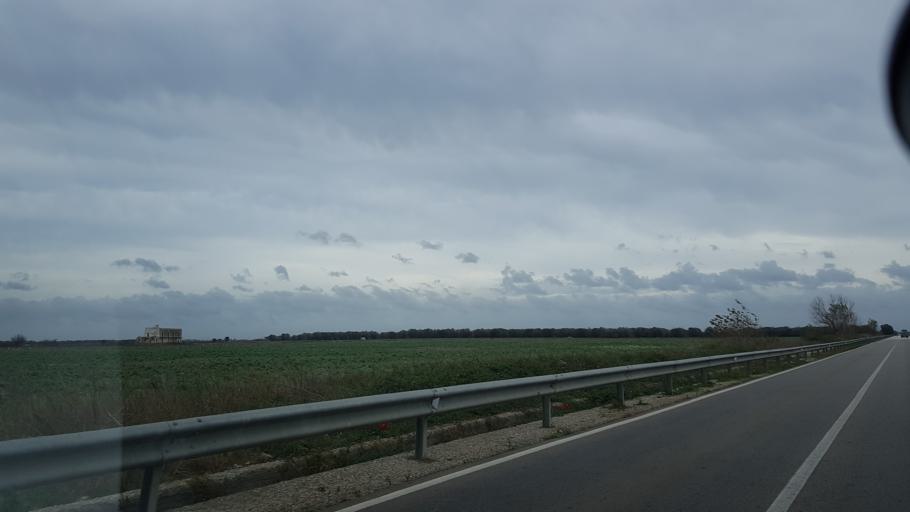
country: IT
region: Apulia
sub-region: Provincia di Brindisi
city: San Pancrazio Salentino
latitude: 40.4098
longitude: 17.8741
